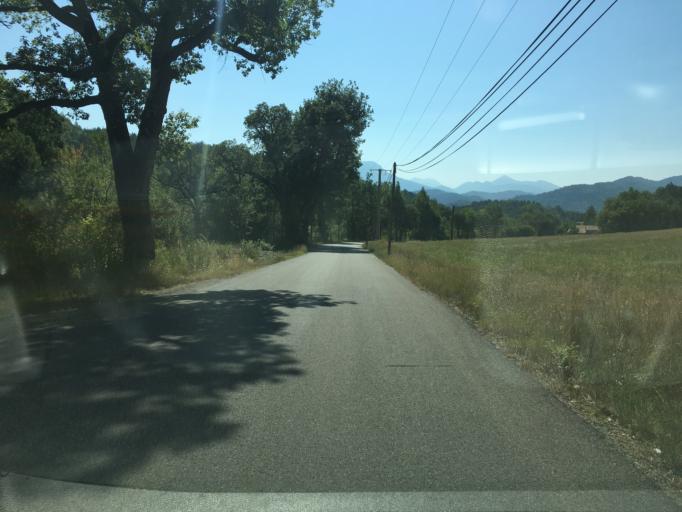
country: FR
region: Provence-Alpes-Cote d'Azur
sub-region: Departement des Alpes-de-Haute-Provence
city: Mallemoisson
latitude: 44.0630
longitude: 6.1469
